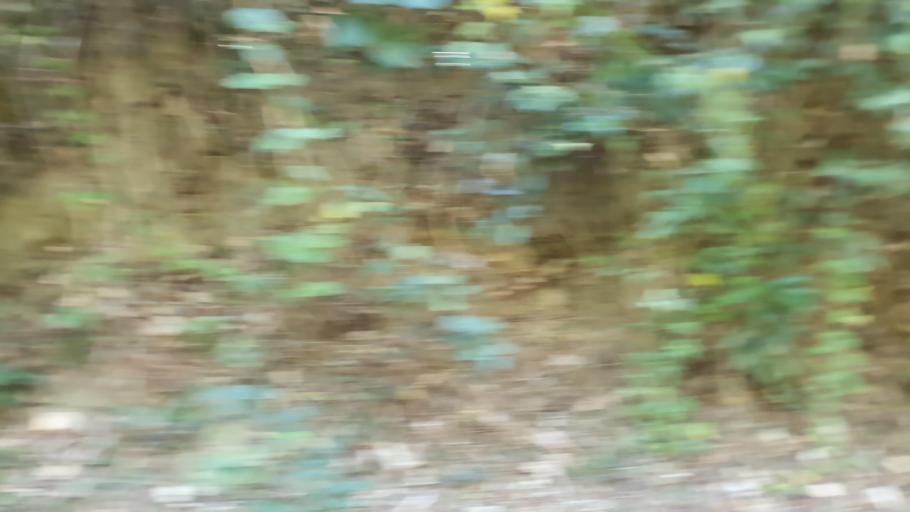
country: TW
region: Taiwan
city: Yujing
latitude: 23.0264
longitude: 120.3903
